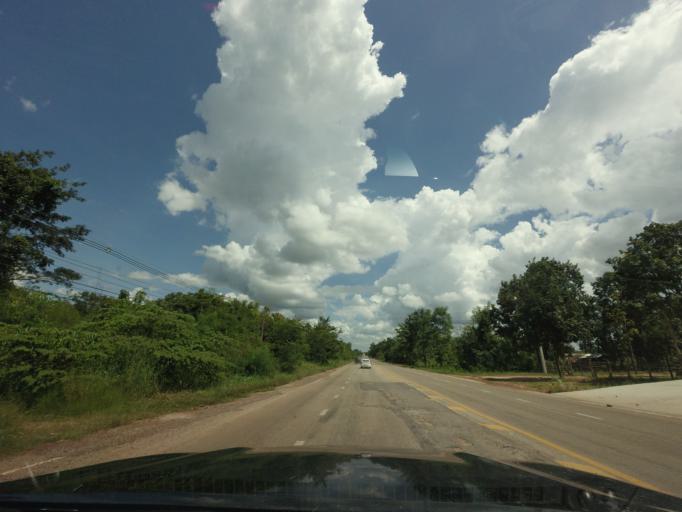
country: TH
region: Changwat Udon Thani
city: Ban Dung
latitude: 17.6833
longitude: 103.2172
